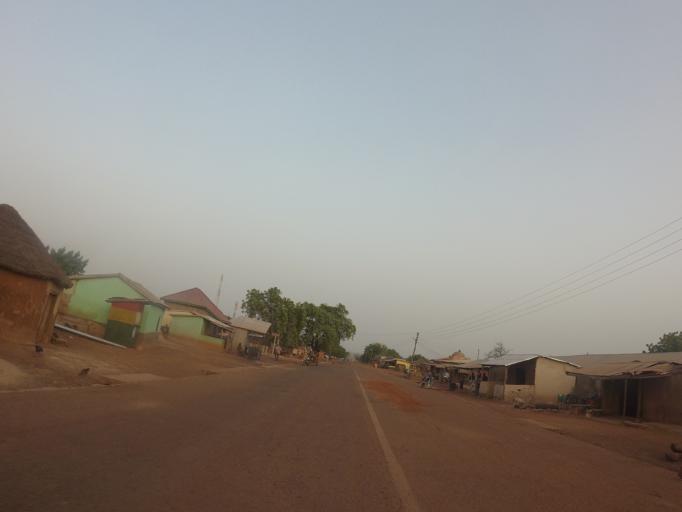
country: GH
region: Northern
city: Tamale
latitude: 9.4451
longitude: -1.1162
